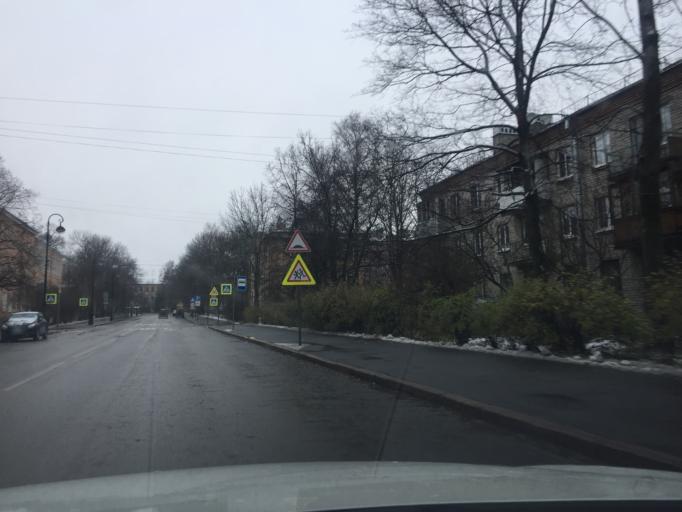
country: RU
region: St.-Petersburg
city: Pushkin
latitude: 59.7227
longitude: 30.4034
